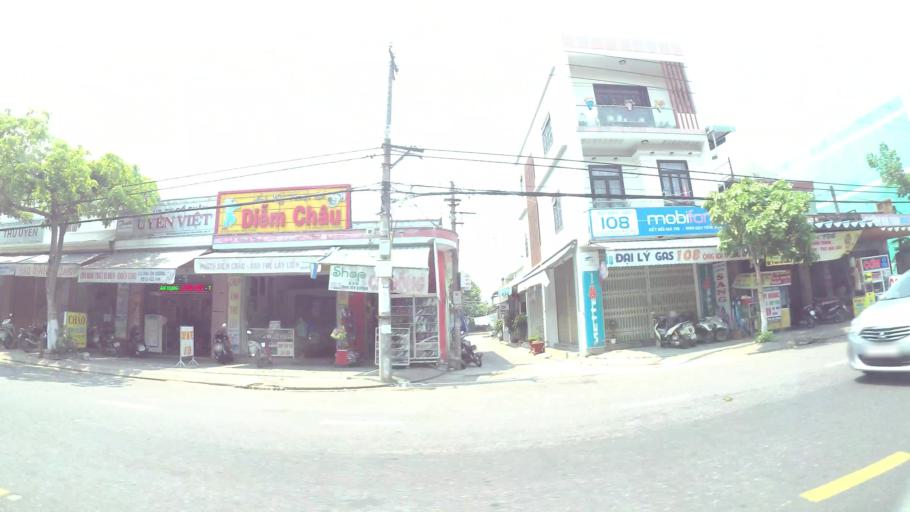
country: VN
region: Da Nang
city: Cam Le
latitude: 16.0147
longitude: 108.2053
